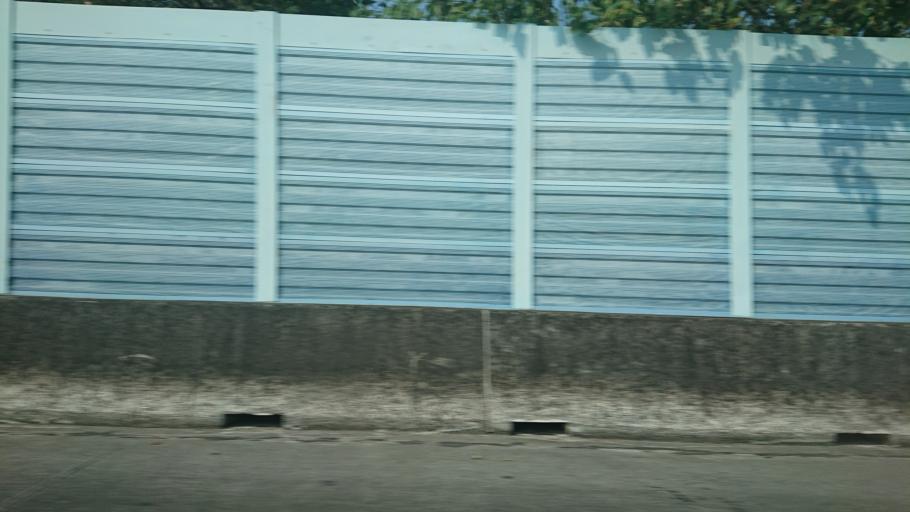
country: TW
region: Taiwan
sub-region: Nantou
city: Nantou
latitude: 23.8915
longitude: 120.7107
